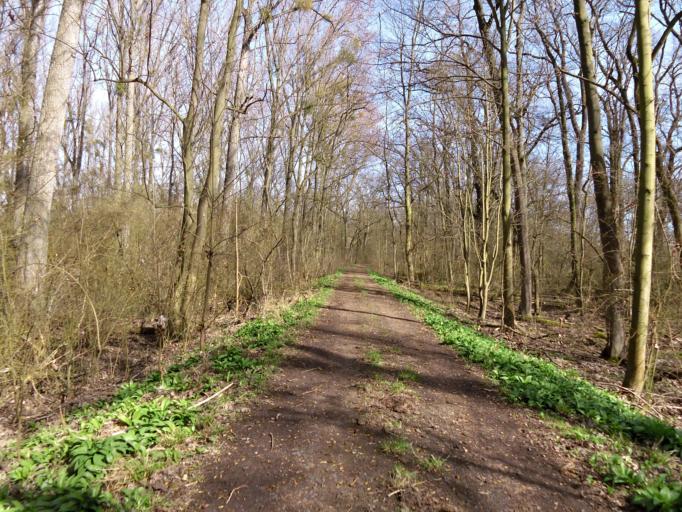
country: DE
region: Hesse
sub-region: Regierungsbezirk Darmstadt
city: Stockstadt am Rhein
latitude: 49.8223
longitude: 8.4242
